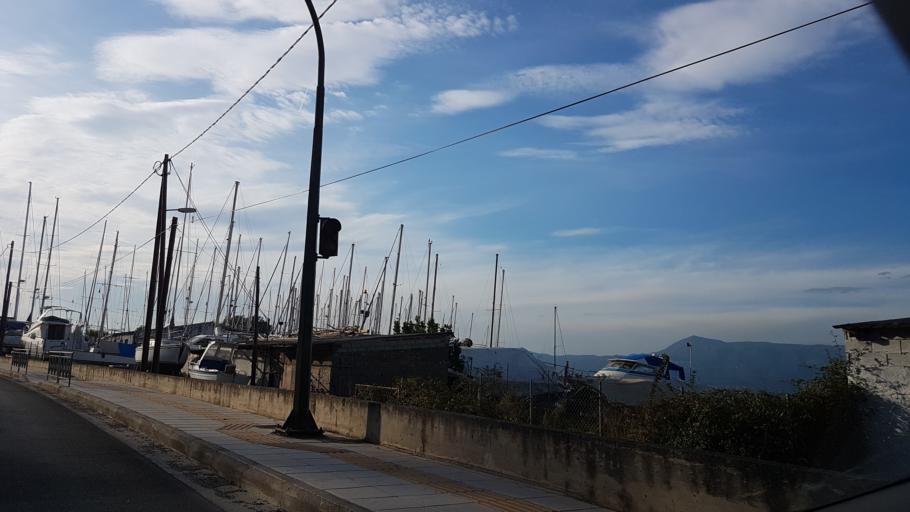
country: GR
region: Ionian Islands
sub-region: Nomos Kerkyras
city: Alepou
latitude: 39.6303
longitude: 19.8986
